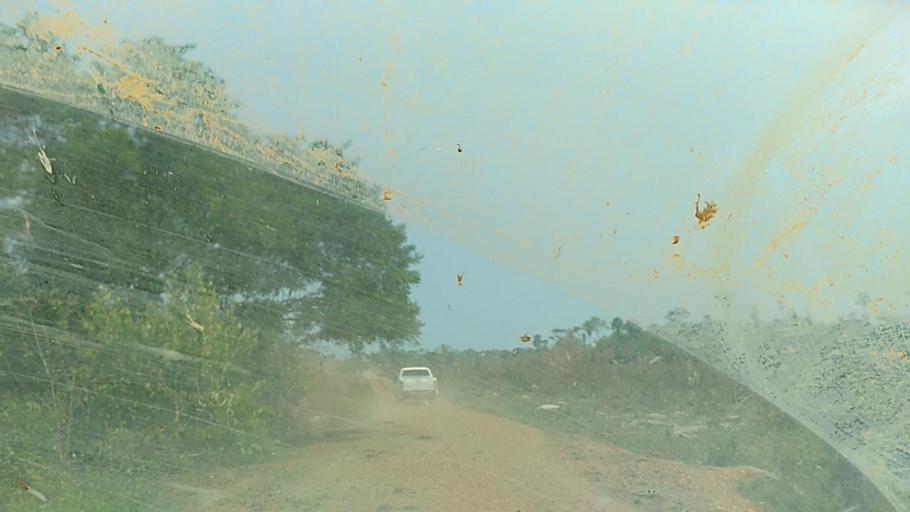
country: BR
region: Rondonia
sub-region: Porto Velho
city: Porto Velho
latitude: -8.9640
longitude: -64.3960
